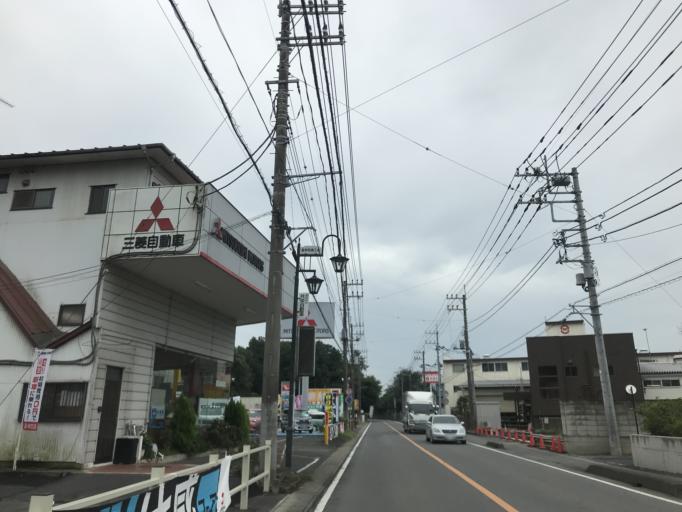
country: JP
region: Ibaraki
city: Koga
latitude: 36.1760
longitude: 139.7636
